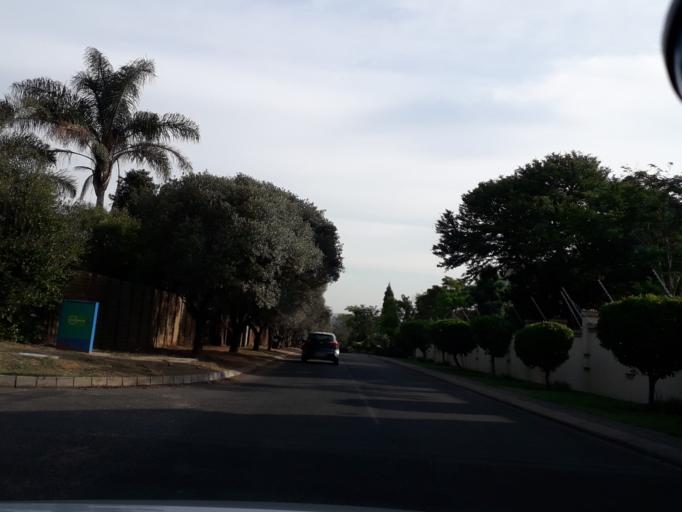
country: ZA
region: Gauteng
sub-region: City of Johannesburg Metropolitan Municipality
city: Diepsloot
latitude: -26.0315
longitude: 27.9910
